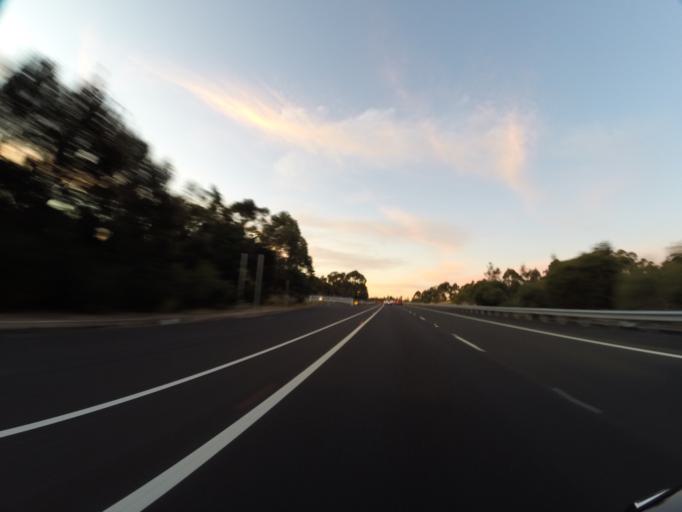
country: AU
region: New South Wales
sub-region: Wollongong
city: Helensburgh
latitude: -34.1524
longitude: 150.9888
